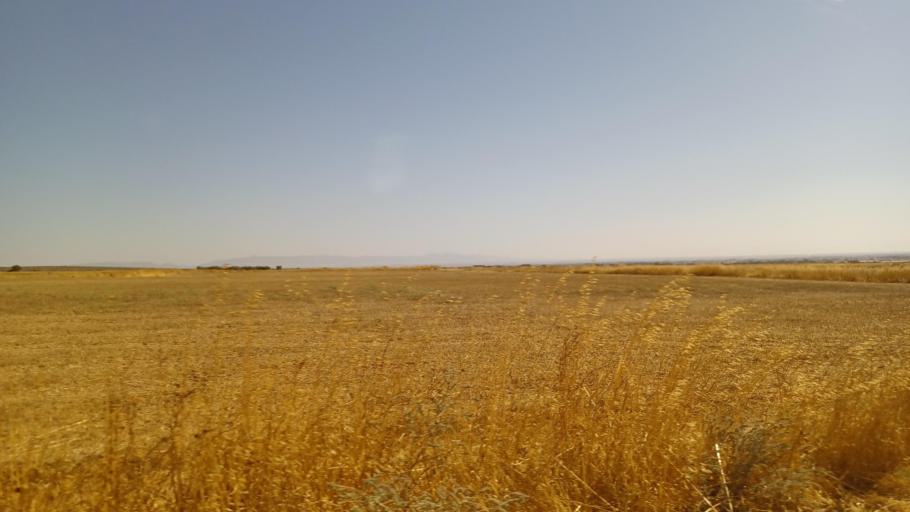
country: CY
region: Larnaka
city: Pergamos
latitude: 35.0435
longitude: 33.6796
